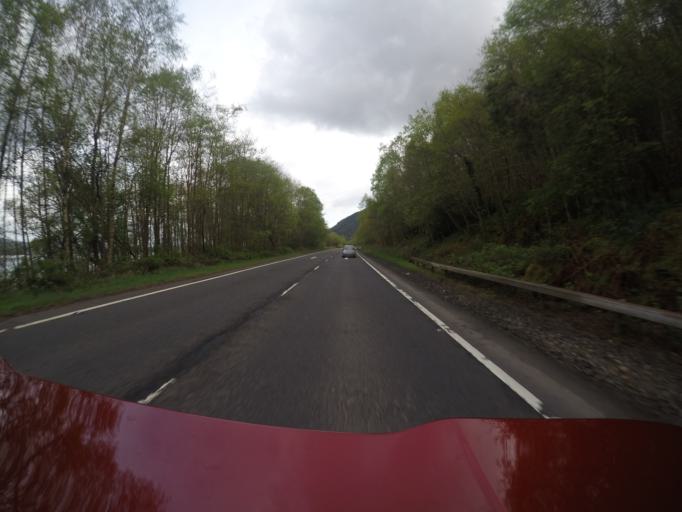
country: GB
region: Scotland
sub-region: Argyll and Bute
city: Helensburgh
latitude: 56.1290
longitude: -4.6547
